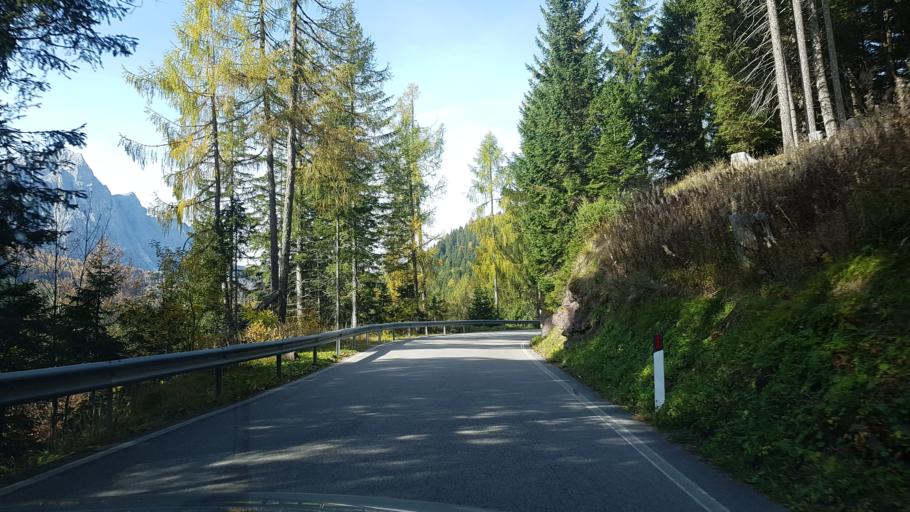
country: IT
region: Veneto
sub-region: Provincia di Belluno
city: Candide
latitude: 46.6500
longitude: 12.4476
